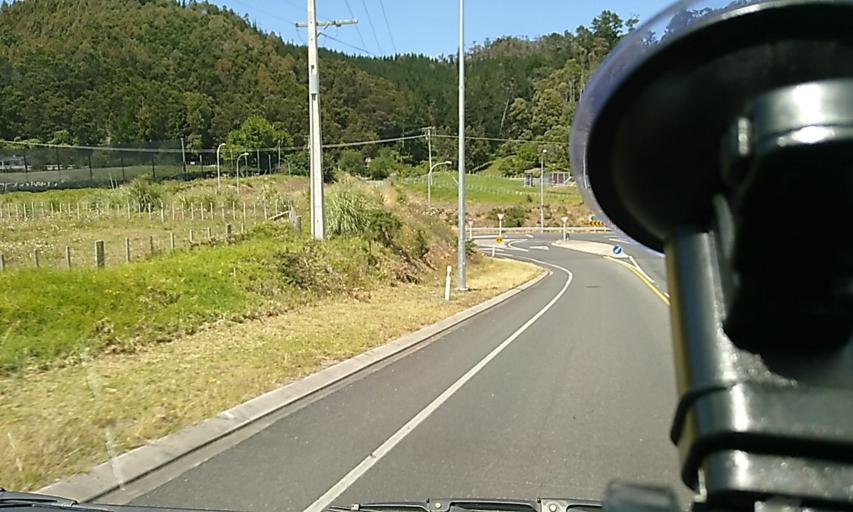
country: NZ
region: Bay of Plenty
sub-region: Western Bay of Plenty District
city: Waihi Beach
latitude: -37.4589
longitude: 175.9307
